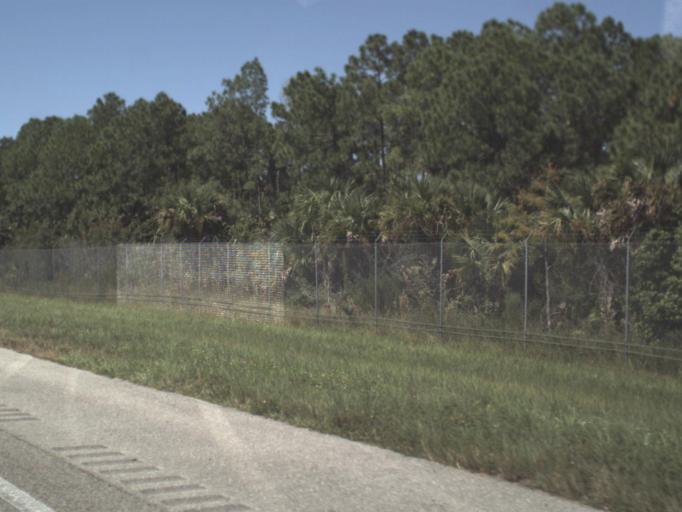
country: US
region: Florida
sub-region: Collier County
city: Orangetree
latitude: 26.1534
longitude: -81.4874
